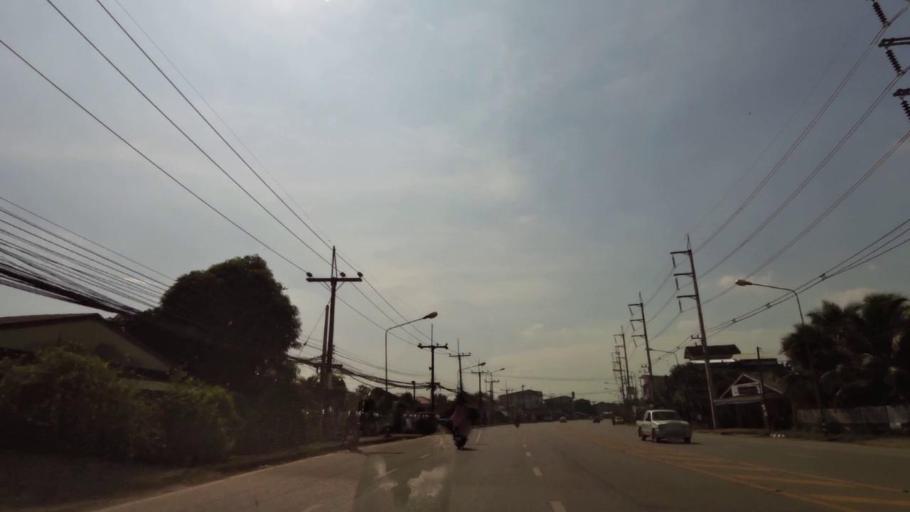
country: TH
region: Chiang Rai
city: Chiang Rai
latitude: 19.8849
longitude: 99.8001
